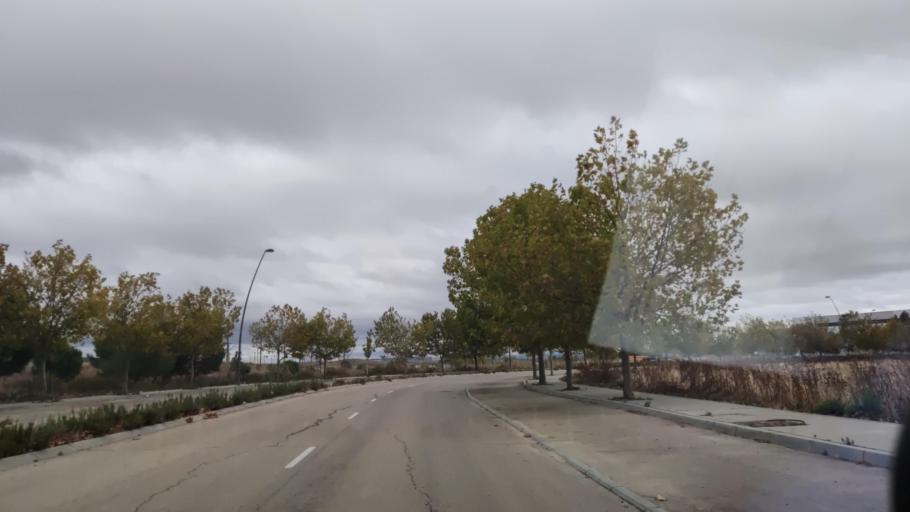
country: ES
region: Madrid
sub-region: Provincia de Madrid
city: Pinto
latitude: 40.2880
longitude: -3.6848
